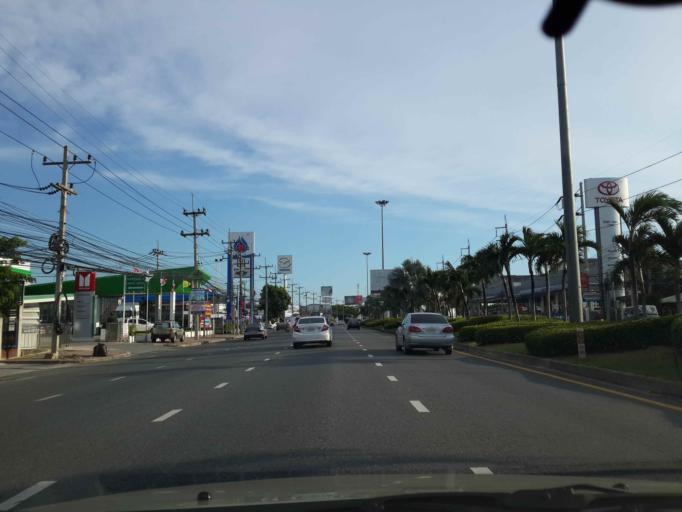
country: TH
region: Chon Buri
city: Bang Lamung
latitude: 12.9902
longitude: 100.9251
